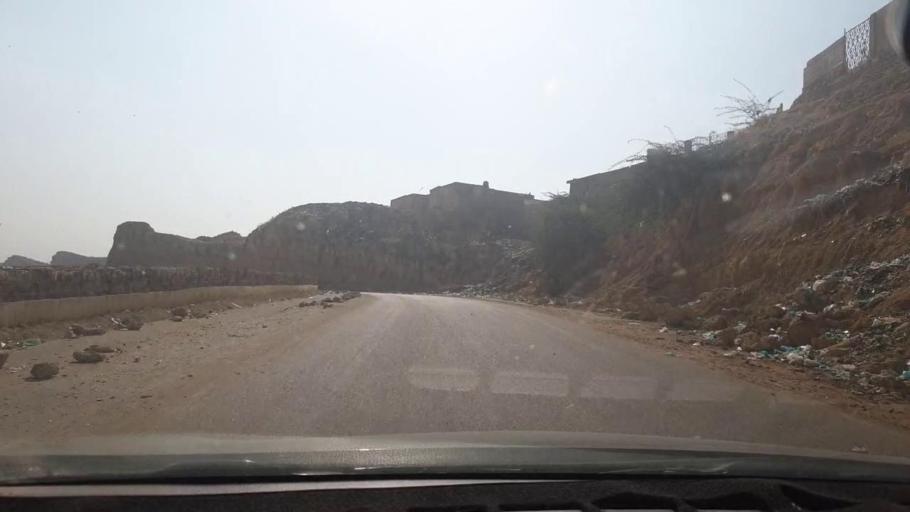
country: PK
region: Sindh
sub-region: Karachi District
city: Karachi
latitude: 24.9722
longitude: 66.9979
